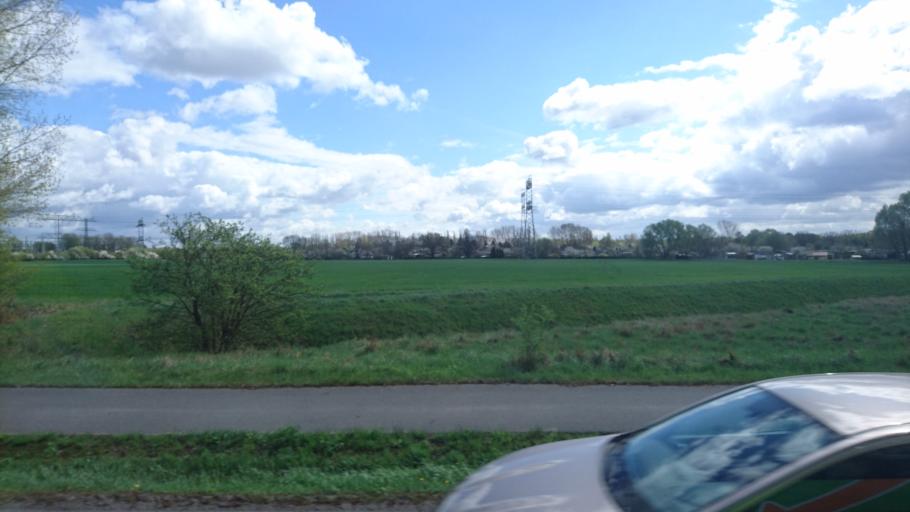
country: DE
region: Berlin
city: Stadtrandsiedlung Malchow
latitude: 52.5896
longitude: 13.4879
